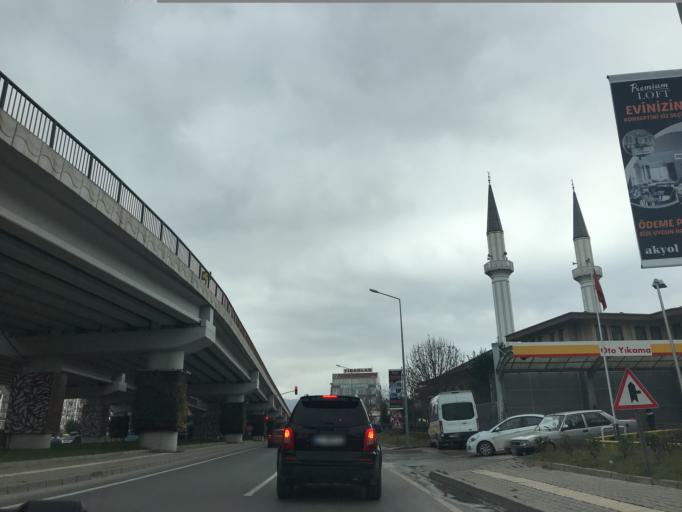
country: TR
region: Yalova
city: Yalova
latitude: 40.6558
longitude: 29.2836
